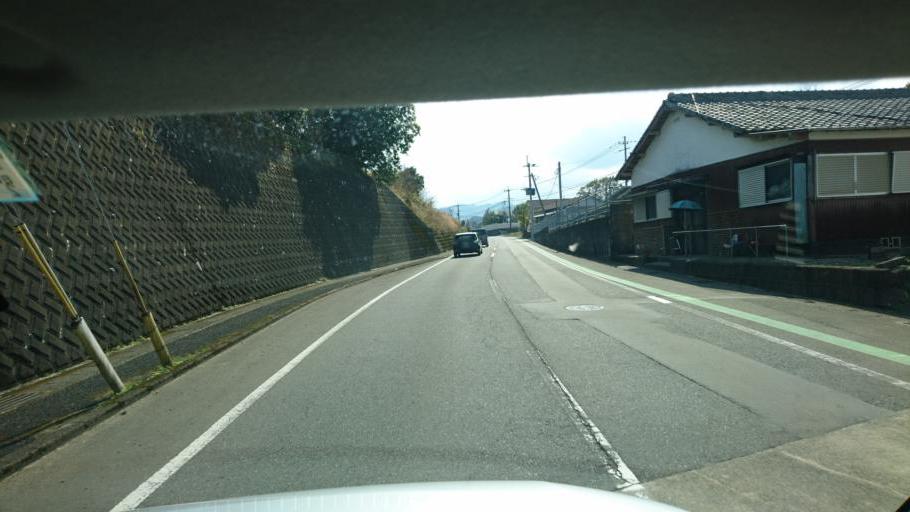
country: JP
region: Miyazaki
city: Miyazaki-shi
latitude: 31.8450
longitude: 131.3938
